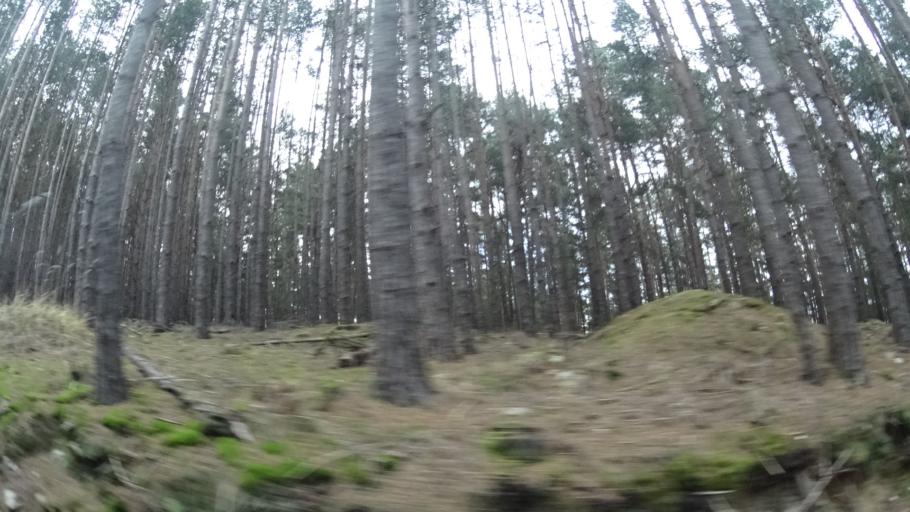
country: DE
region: Thuringia
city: Orlamunde
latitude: 50.7484
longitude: 11.4675
